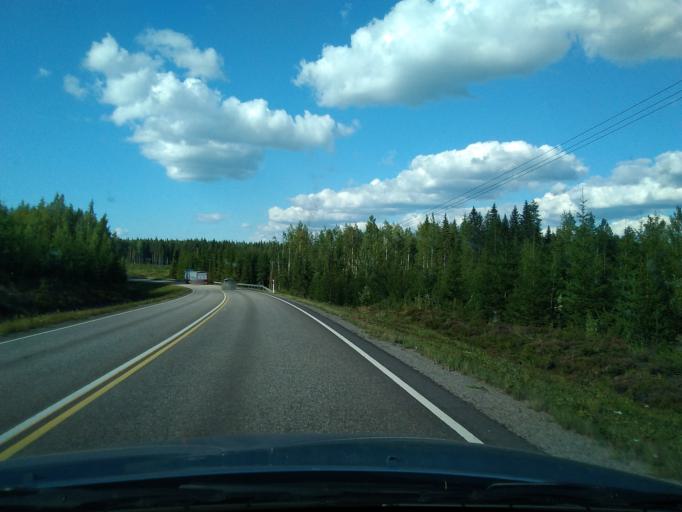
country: FI
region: Pirkanmaa
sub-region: Ylae-Pirkanmaa
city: Maenttae
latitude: 62.1163
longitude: 24.7446
